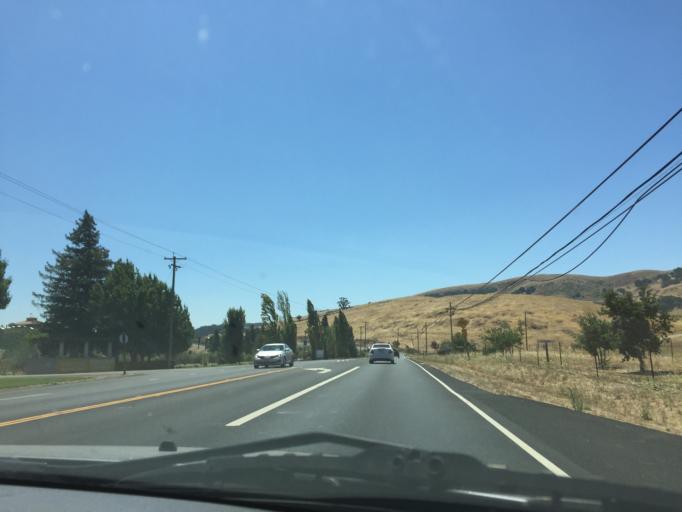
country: US
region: California
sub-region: Sonoma County
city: Temelec
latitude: 38.2130
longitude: -122.4551
